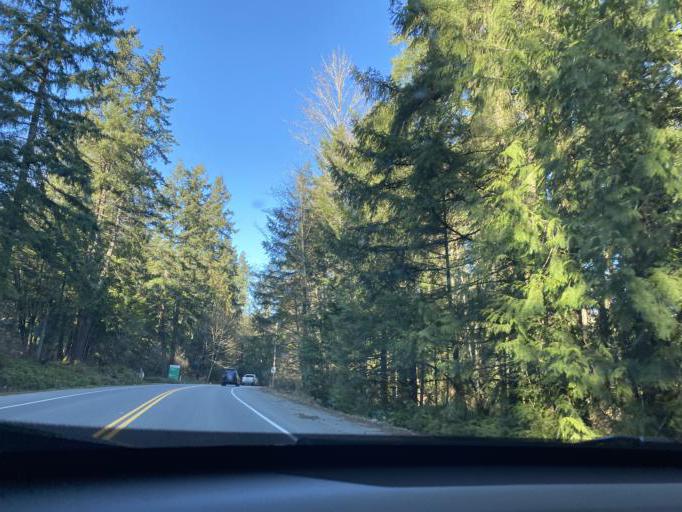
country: US
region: Washington
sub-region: King County
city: Federal Way
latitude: 47.3081
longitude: -122.2922
